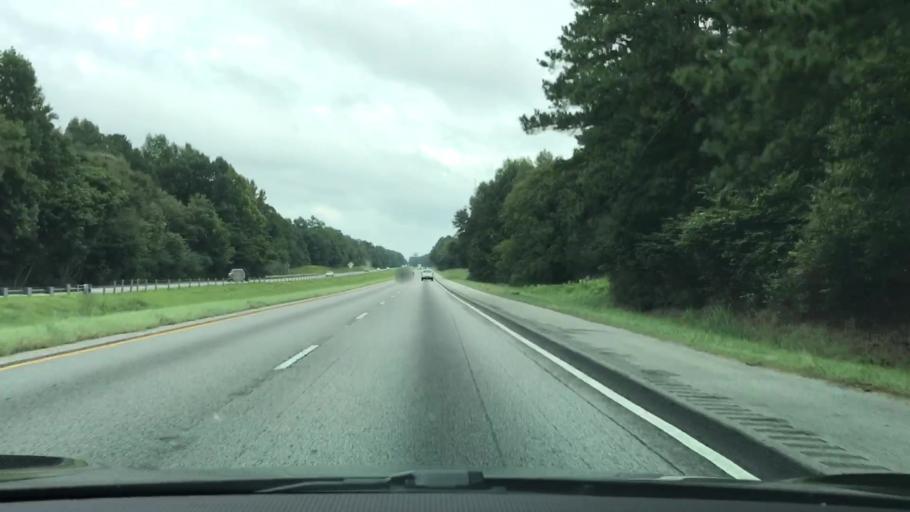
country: US
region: Alabama
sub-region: Lee County
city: Auburn
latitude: 32.5331
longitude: -85.5547
